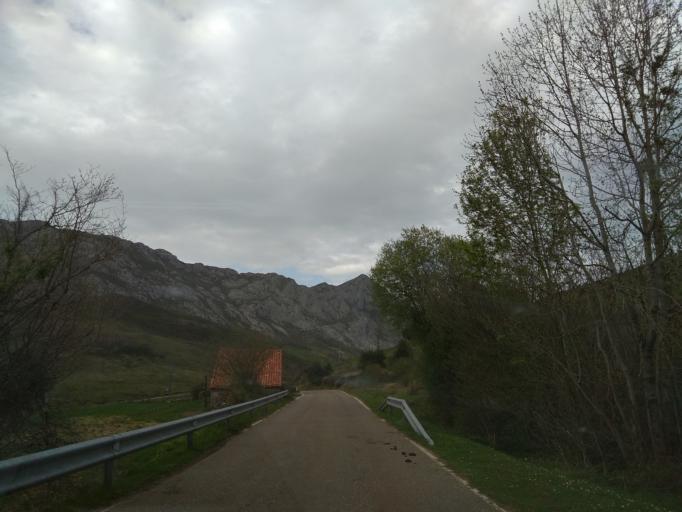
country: ES
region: Cantabria
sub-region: Provincia de Cantabria
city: Cabezon de Liebana
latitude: 43.2482
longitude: -4.5389
